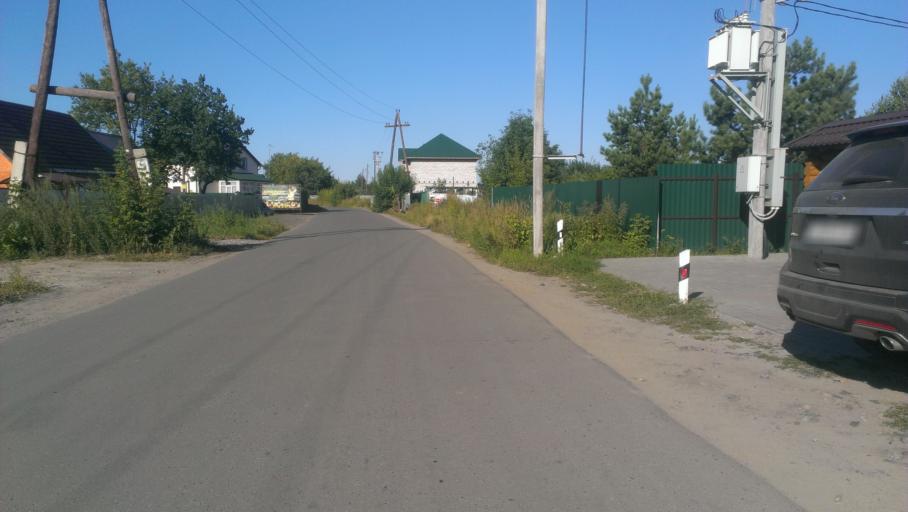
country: RU
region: Altai Krai
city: Novosilikatnyy
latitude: 53.3209
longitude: 83.6793
